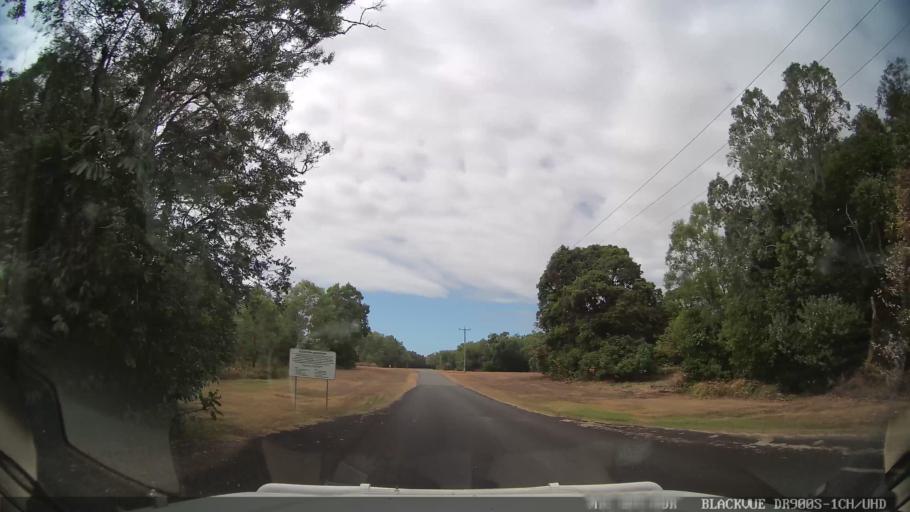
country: AU
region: Queensland
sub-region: Cook
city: Cooktown
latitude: -15.4459
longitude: 145.1794
